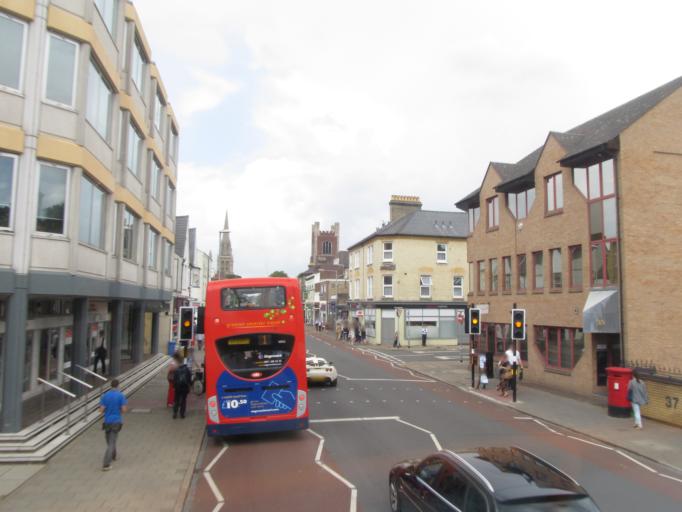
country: GB
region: England
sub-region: Cambridgeshire
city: Cambridge
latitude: 52.1962
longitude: 0.1301
